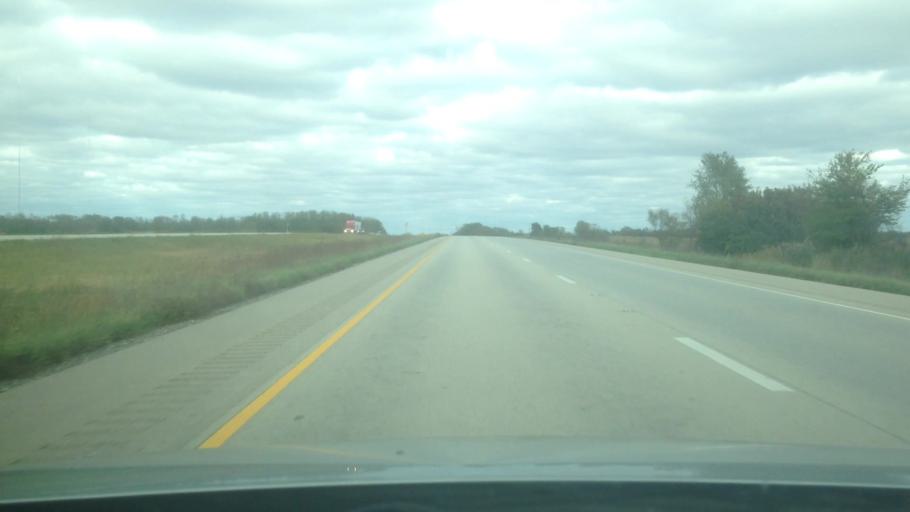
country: US
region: Illinois
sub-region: Macon County
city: Forsyth
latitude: 39.9253
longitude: -88.8508
